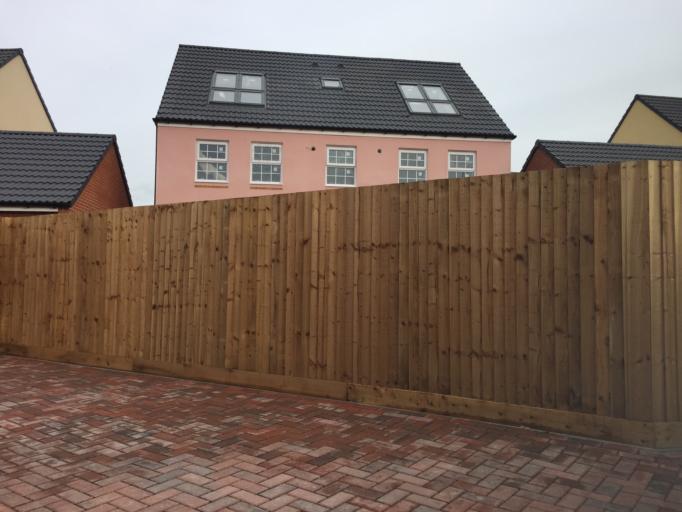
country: GB
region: England
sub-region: South Gloucestershire
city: Thornbury
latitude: 51.6213
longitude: -2.5264
